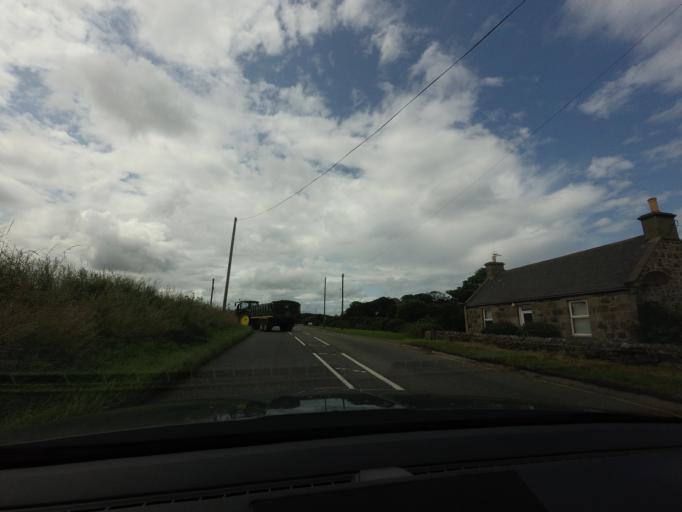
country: GB
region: Scotland
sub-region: Aberdeenshire
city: Whitehills
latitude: 57.6646
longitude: -2.5623
